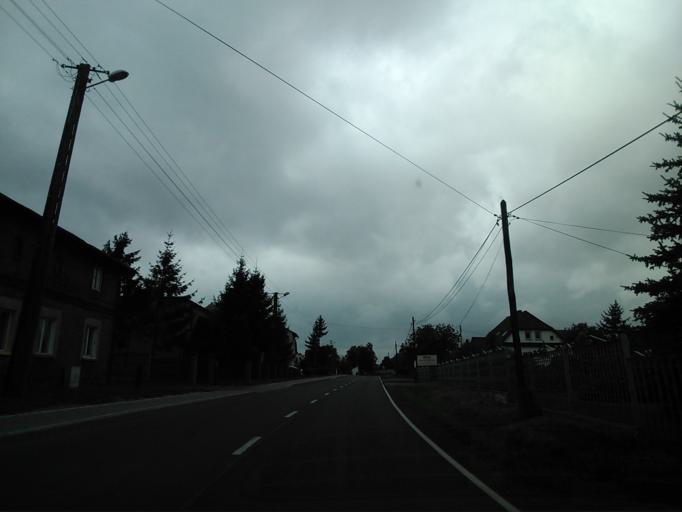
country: PL
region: Kujawsko-Pomorskie
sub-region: Powiat inowroclawski
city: Kruszwica
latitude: 52.6826
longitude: 18.2703
